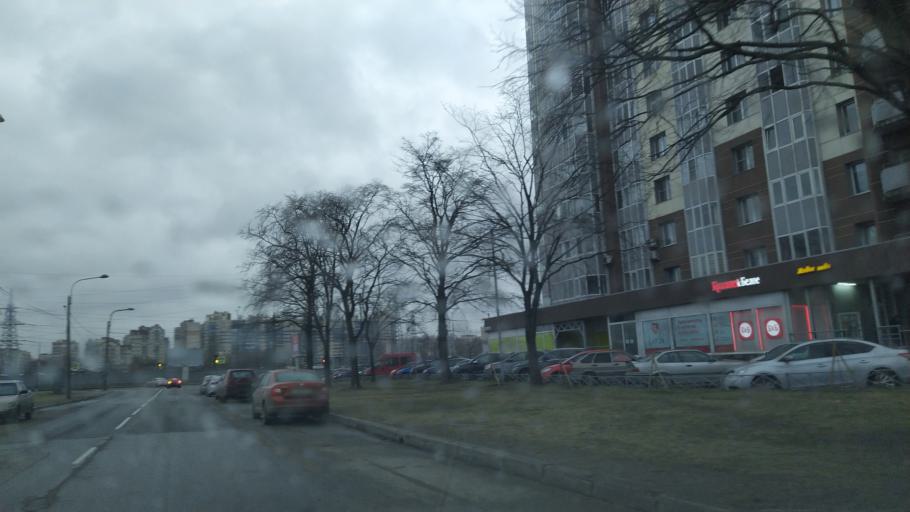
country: RU
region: Leningrad
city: Akademicheskoe
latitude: 60.0242
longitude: 30.3941
